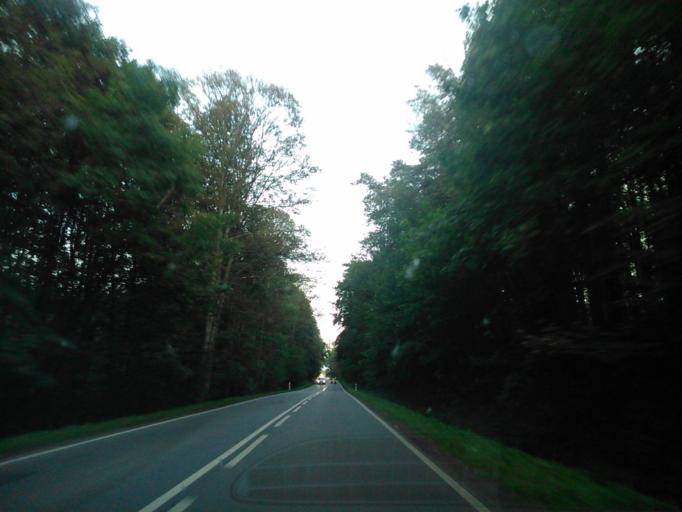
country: PL
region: Kujawsko-Pomorskie
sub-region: Powiat wabrzeski
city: Wabrzezno
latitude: 53.2594
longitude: 19.0080
